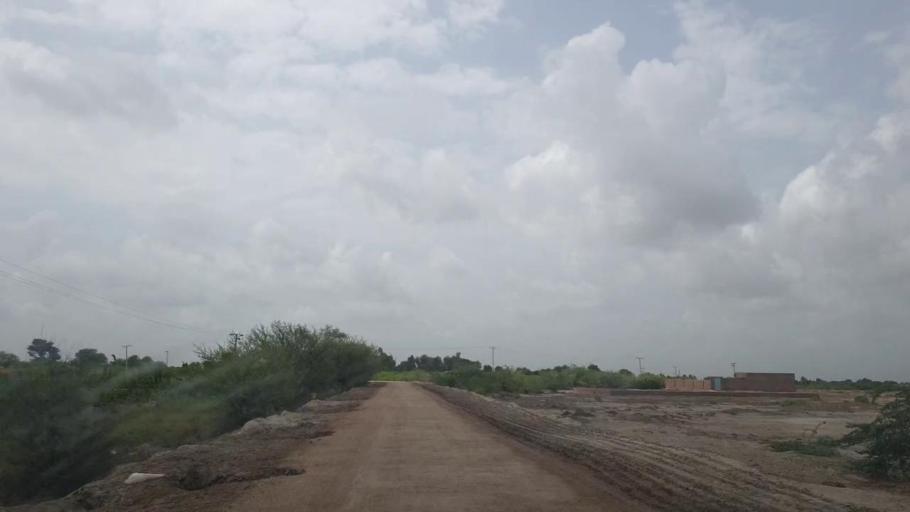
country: PK
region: Sindh
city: Naukot
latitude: 24.9438
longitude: 69.2587
